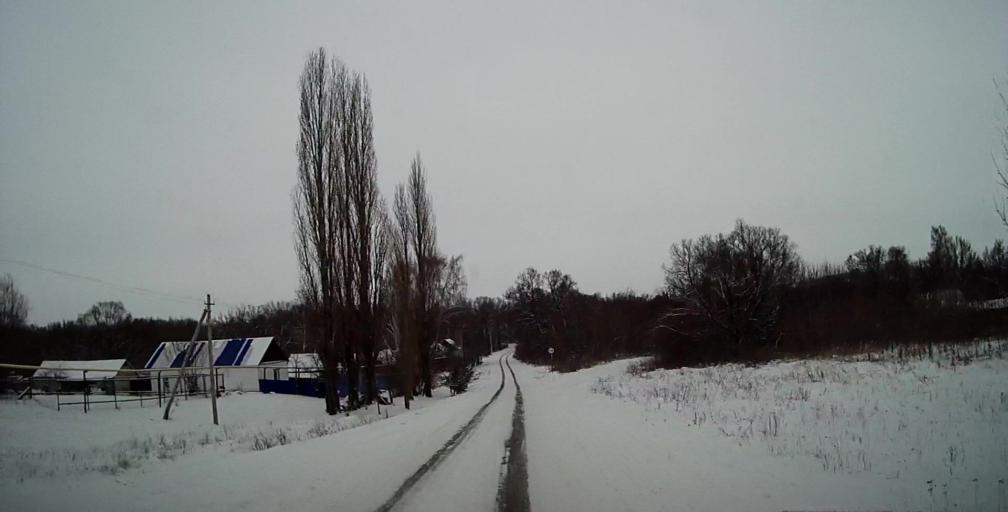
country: RU
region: Lipetsk
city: Lev Tolstoy
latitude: 53.3382
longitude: 39.5841
